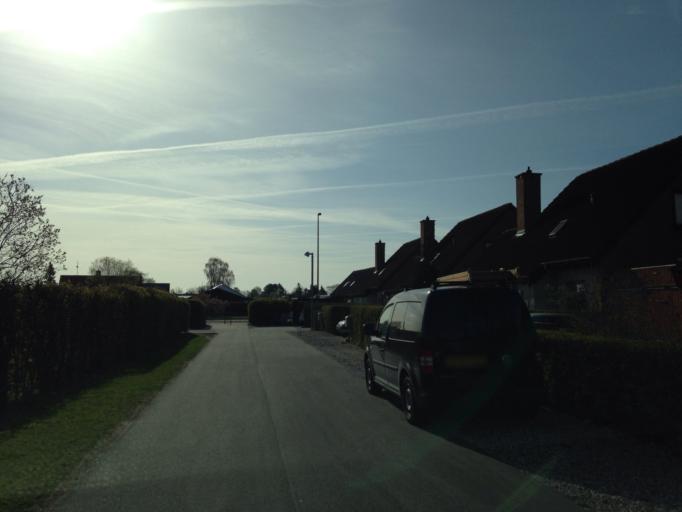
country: DK
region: Zealand
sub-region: Greve Kommune
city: Greve
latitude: 55.5869
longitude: 12.2972
